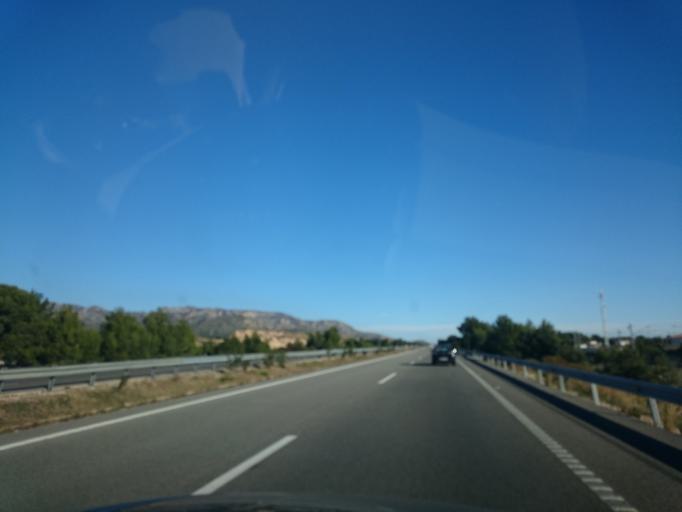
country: ES
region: Catalonia
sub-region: Provincia de Tarragona
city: l'Ametlla de Mar
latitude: 40.9253
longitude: 0.8374
